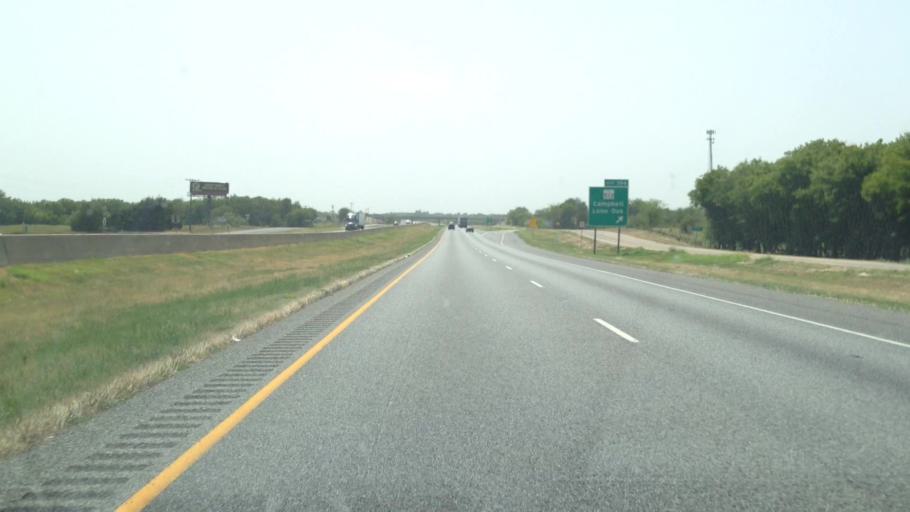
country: US
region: Texas
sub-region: Hunt County
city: Commerce
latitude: 33.1319
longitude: -95.9394
